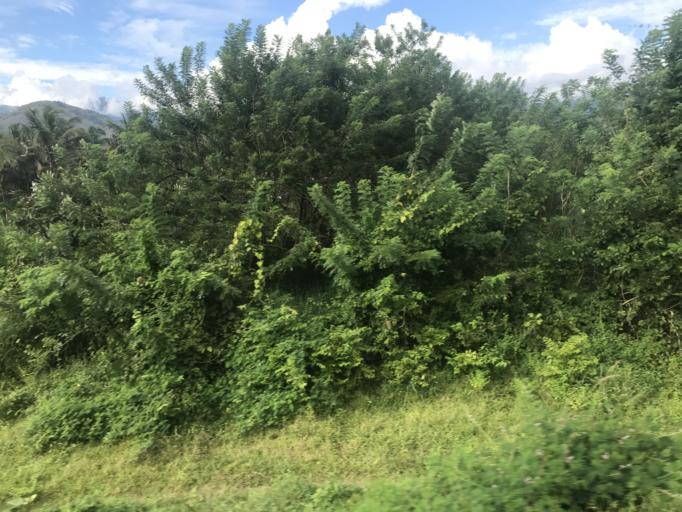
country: IN
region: Kerala
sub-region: Palakkad district
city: Palakkad
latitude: 10.8155
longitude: 76.6790
